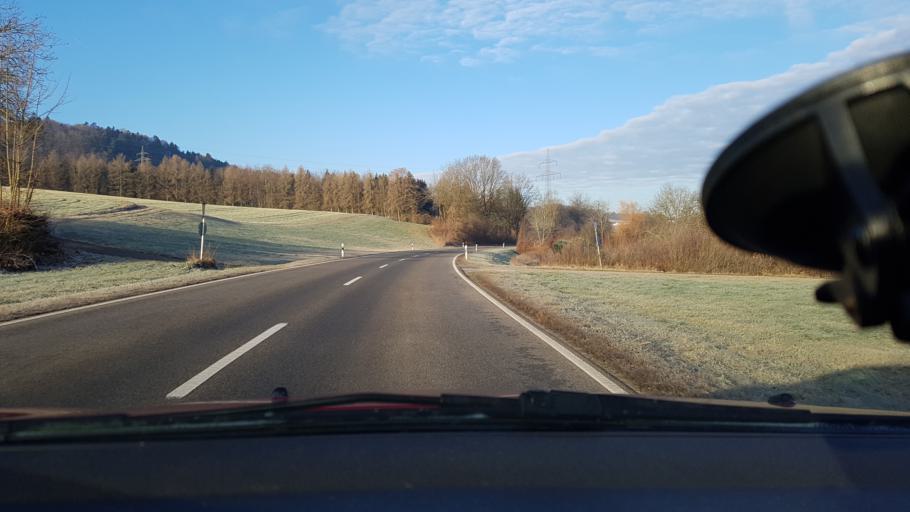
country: DE
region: Bavaria
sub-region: Lower Bavaria
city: Simbach am Inn
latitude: 48.2735
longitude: 13.0051
